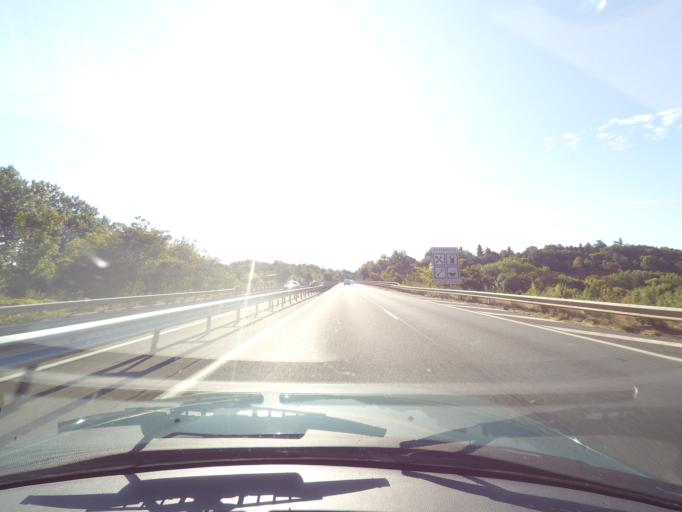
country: FR
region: Poitou-Charentes
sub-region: Departement de la Vienne
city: Chasseneuil-du-Poitou
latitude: 46.6183
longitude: 0.3572
